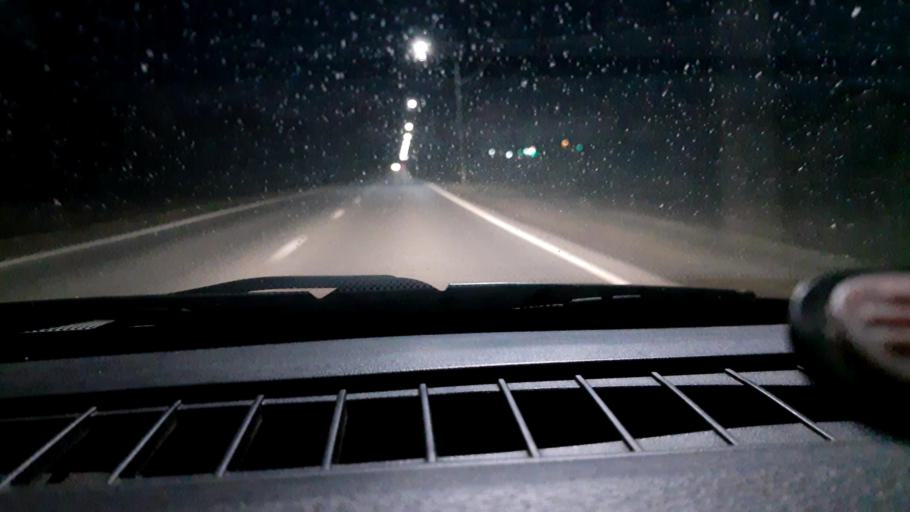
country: RU
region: Nizjnij Novgorod
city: Neklyudovo
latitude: 56.3786
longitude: 44.0114
